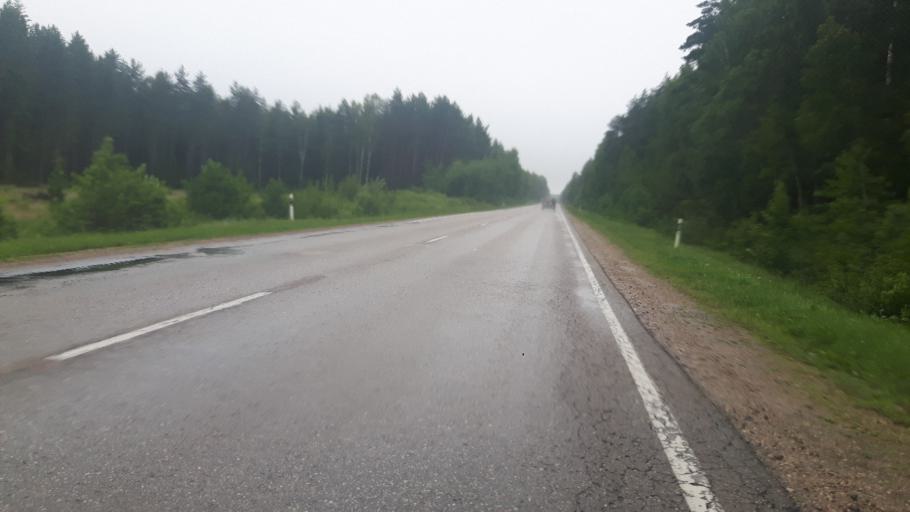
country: LV
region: Rucavas
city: Rucava
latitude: 56.1179
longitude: 21.1436
